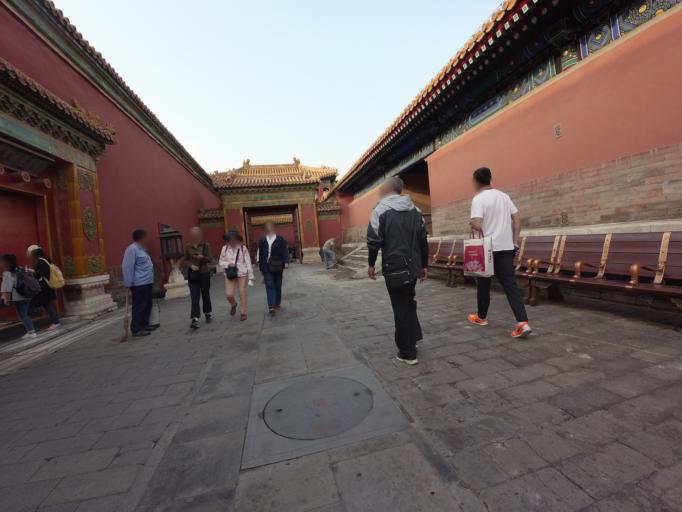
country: CN
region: Beijing
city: Beijing
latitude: 39.9195
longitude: 116.3899
